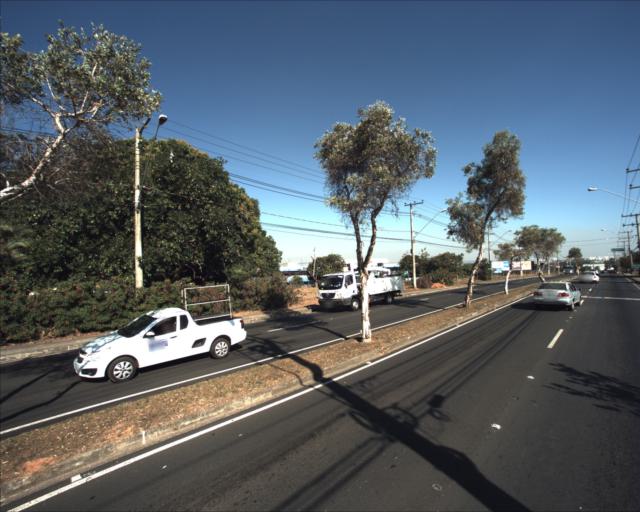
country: BR
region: Sao Paulo
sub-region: Sorocaba
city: Sorocaba
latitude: -23.4577
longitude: -47.4201
